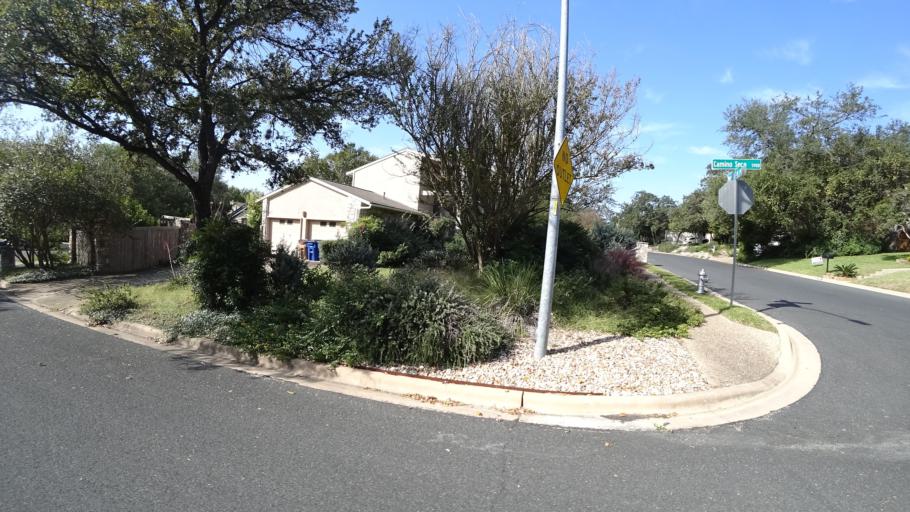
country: US
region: Texas
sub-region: Travis County
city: West Lake Hills
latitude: 30.3439
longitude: -97.7628
